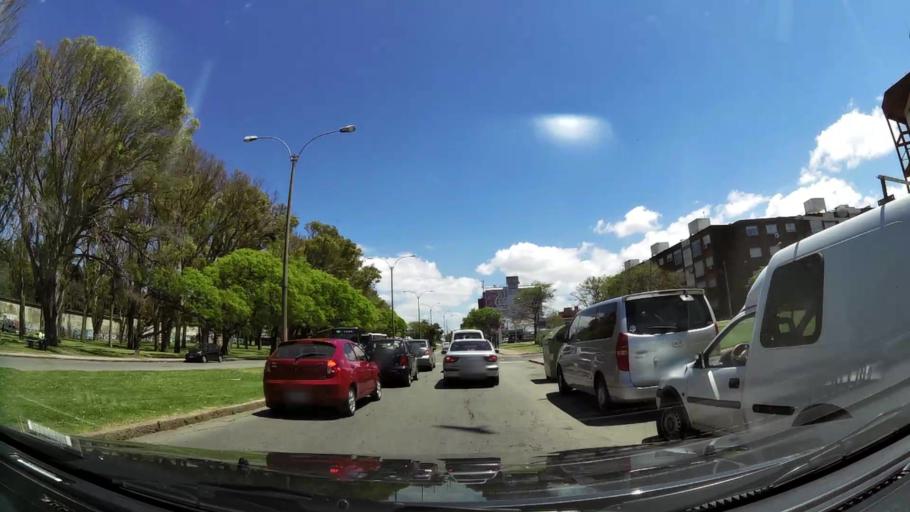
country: UY
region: Montevideo
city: Montevideo
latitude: -34.8985
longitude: -56.1237
